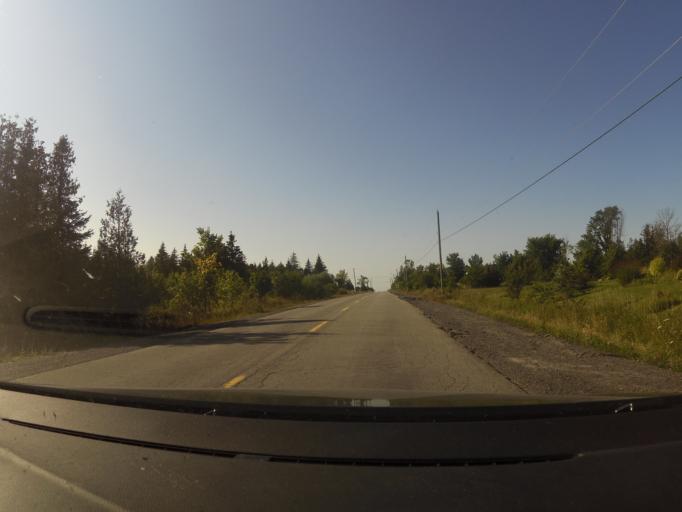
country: CA
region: Ontario
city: Carleton Place
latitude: 45.3042
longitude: -76.0787
